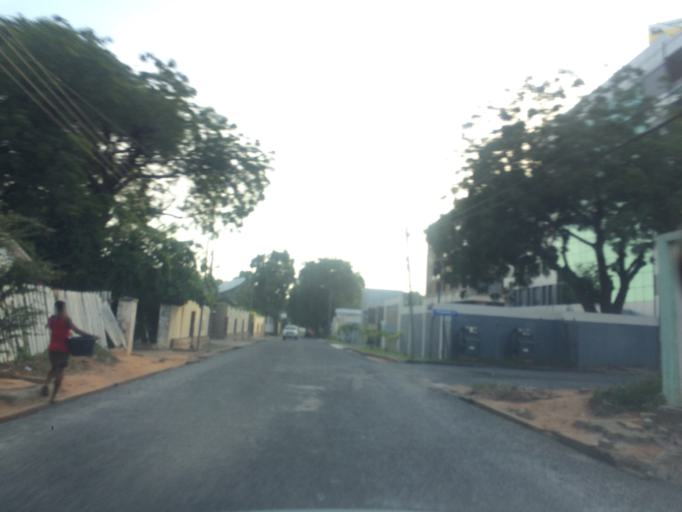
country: GH
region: Greater Accra
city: Accra
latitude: 5.5613
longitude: -0.2026
